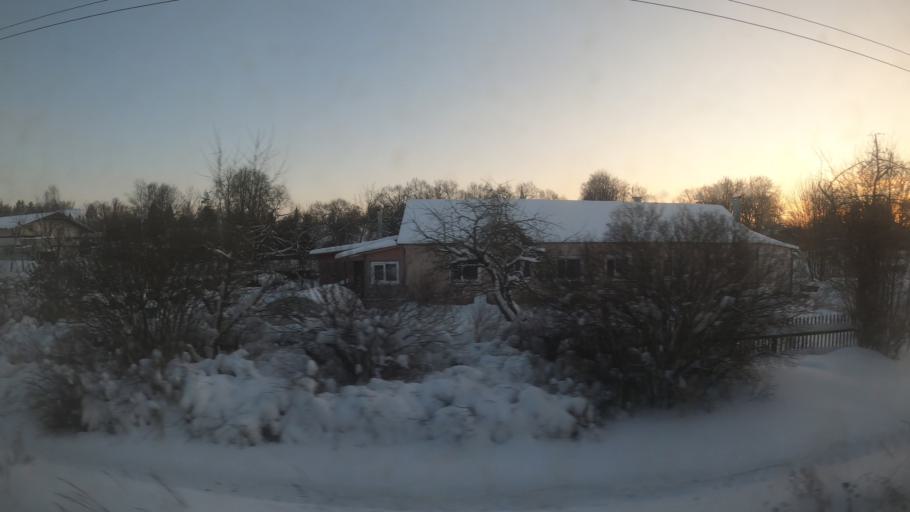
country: RU
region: Moskovskaya
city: Dedenevo
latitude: 56.2407
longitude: 37.5127
